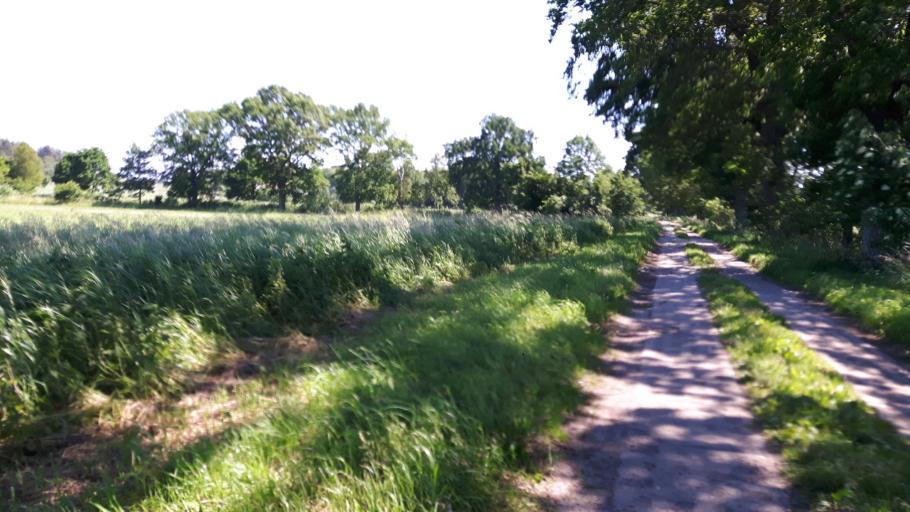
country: PL
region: Pomeranian Voivodeship
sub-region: Powiat slupski
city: Glowczyce
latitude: 54.6412
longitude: 17.3556
